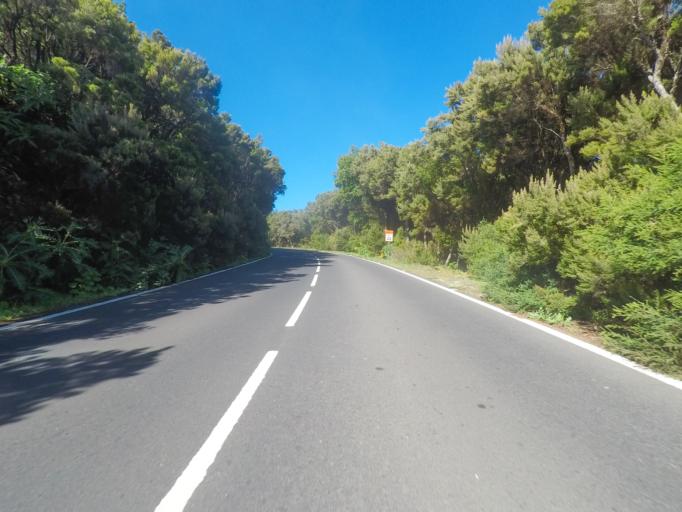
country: ES
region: Canary Islands
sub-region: Provincia de Santa Cruz de Tenerife
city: Alajero
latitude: 28.1074
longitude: -17.2339
